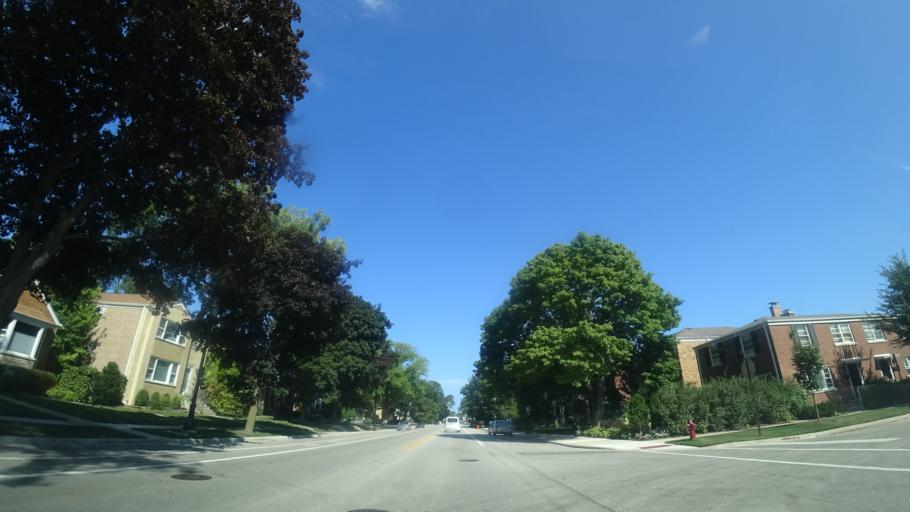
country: US
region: Illinois
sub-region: Cook County
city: Wilmette
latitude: 42.0645
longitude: -87.7220
